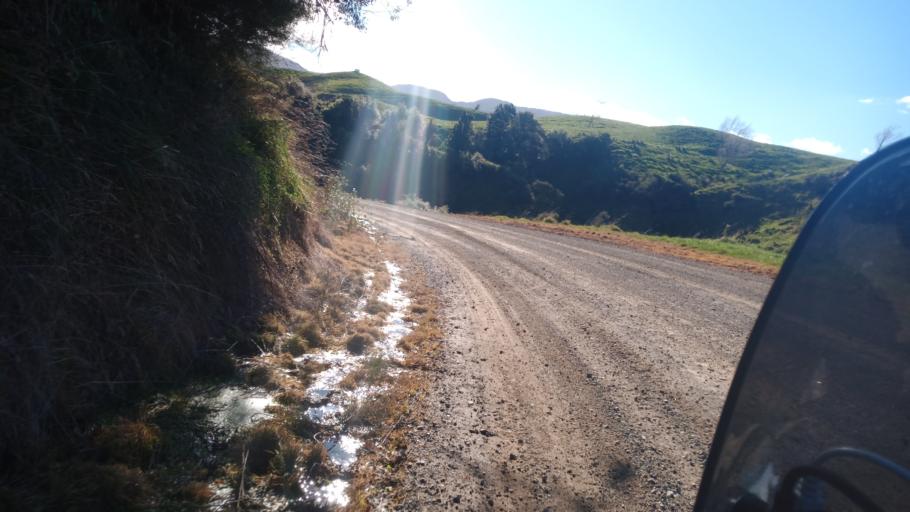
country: NZ
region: Hawke's Bay
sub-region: Wairoa District
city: Wairoa
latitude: -38.7463
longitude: 177.2808
